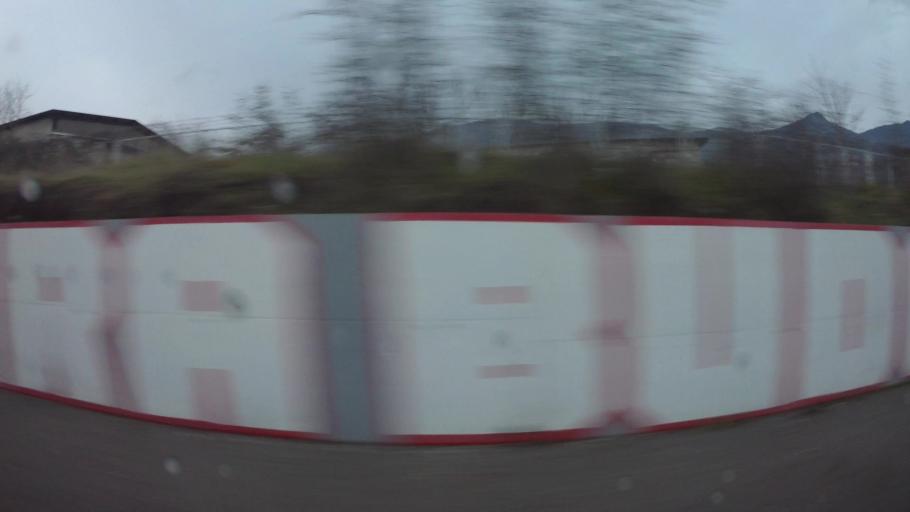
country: BA
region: Federation of Bosnia and Herzegovina
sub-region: Hercegovacko-Bosanski Kanton
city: Mostar
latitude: 43.3593
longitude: 17.8011
